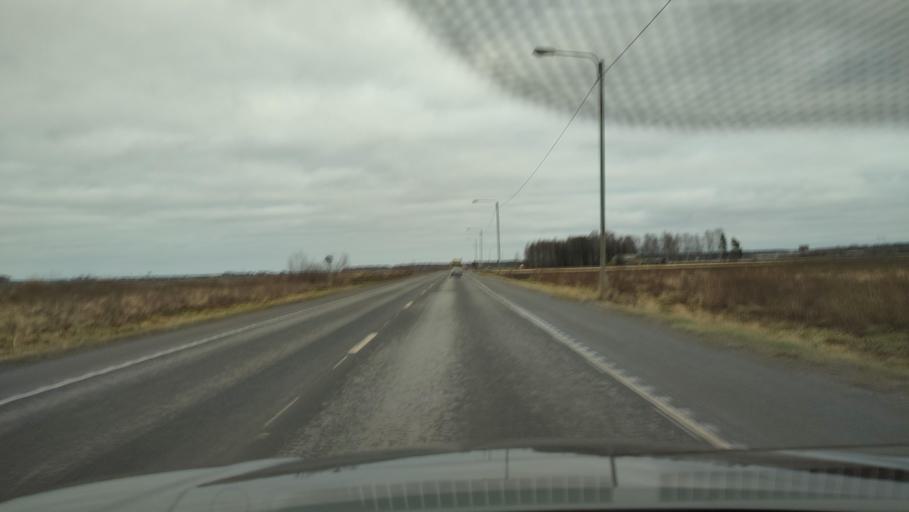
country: FI
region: Southern Ostrobothnia
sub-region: Seinaejoki
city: Ilmajoki
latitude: 62.7357
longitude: 22.6080
